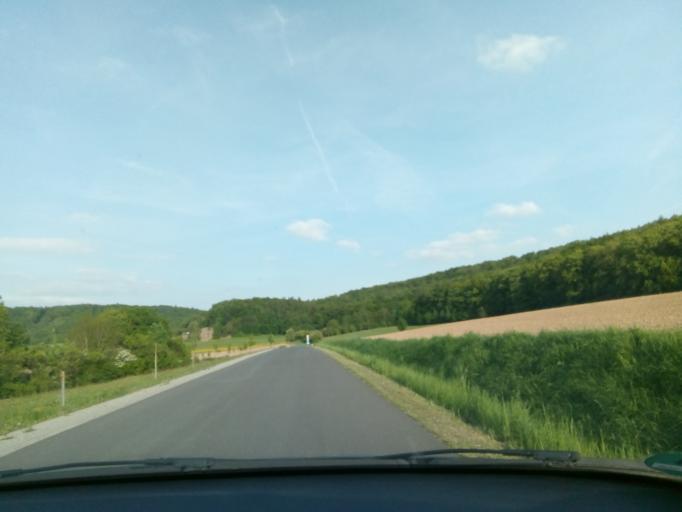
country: DE
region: Bavaria
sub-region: Regierungsbezirk Unterfranken
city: Oberschwarzach
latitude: 49.8682
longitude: 10.4336
